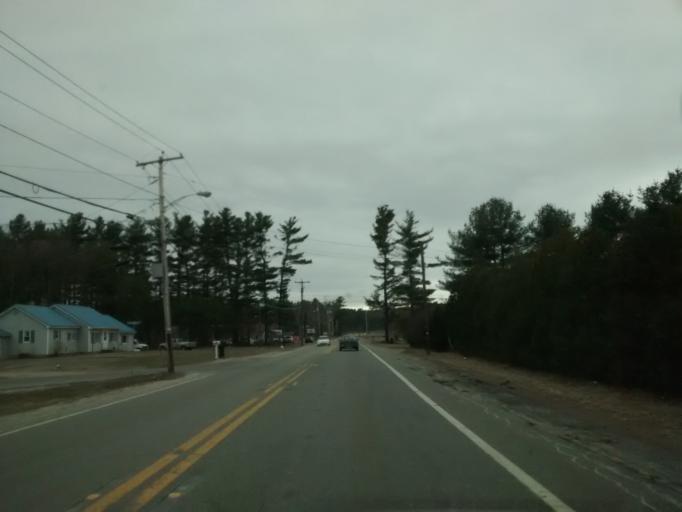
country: US
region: Massachusetts
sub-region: Franklin County
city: Orange
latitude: 42.5568
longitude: -72.2879
